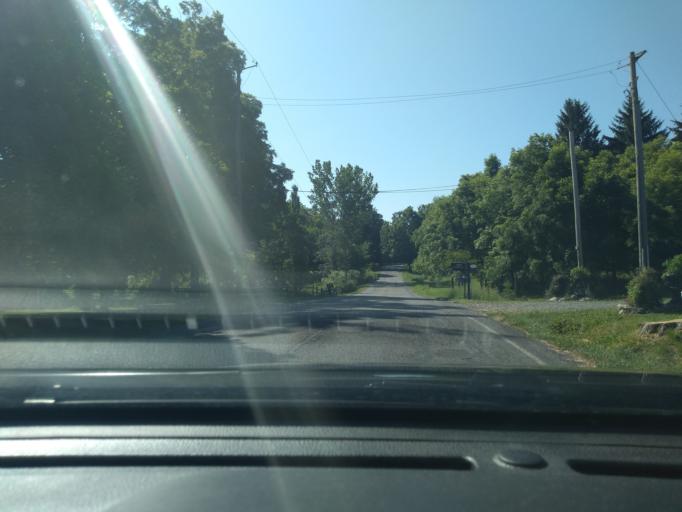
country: US
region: New York
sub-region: Erie County
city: Billington Heights
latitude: 42.7846
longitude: -78.6864
